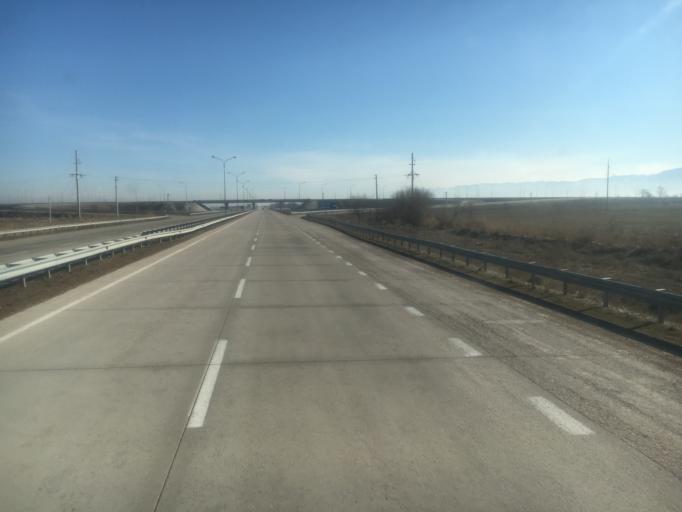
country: KZ
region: Zhambyl
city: Oytal
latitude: 42.9290
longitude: 73.2358
